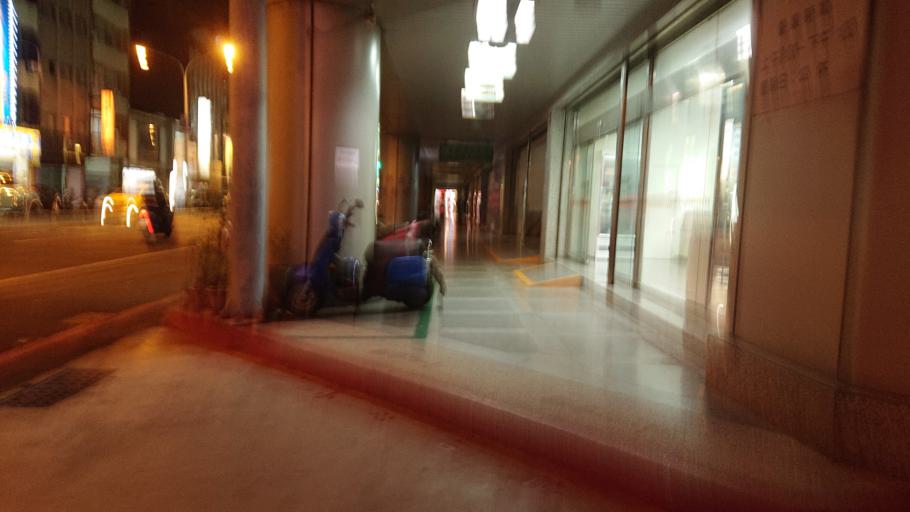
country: TW
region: Taiwan
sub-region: Tainan
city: Tainan
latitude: 22.9951
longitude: 120.1977
